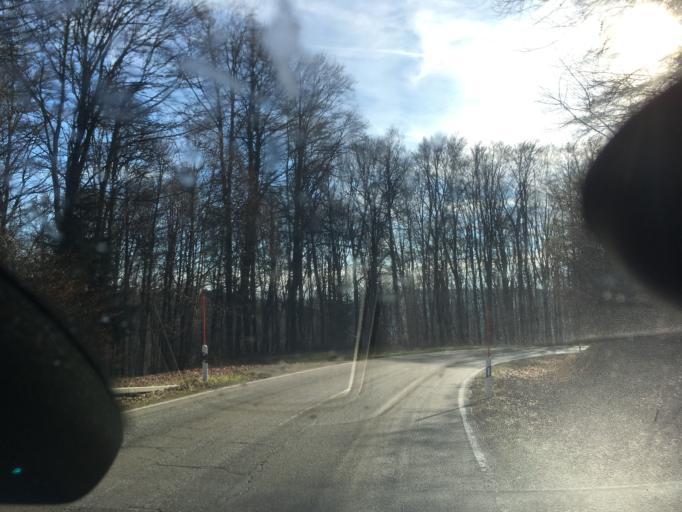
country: DE
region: Baden-Wuerttemberg
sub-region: Freiburg Region
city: Gorwihl
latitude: 47.6338
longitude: 8.0916
